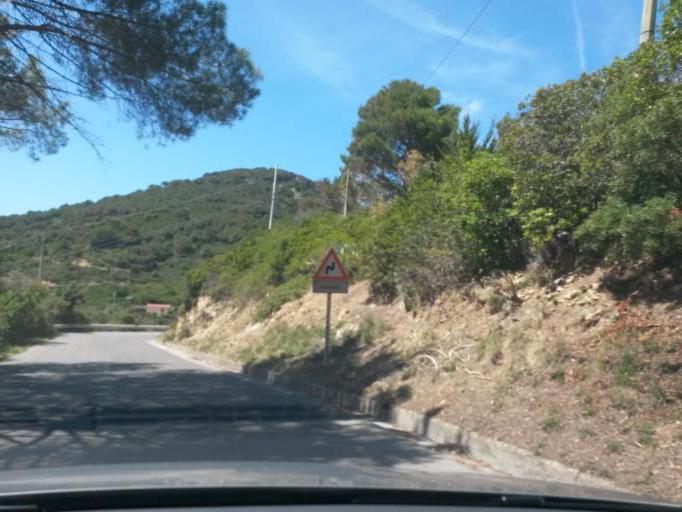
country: IT
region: Tuscany
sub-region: Provincia di Livorno
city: Portoferraio
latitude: 42.8248
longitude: 10.2712
